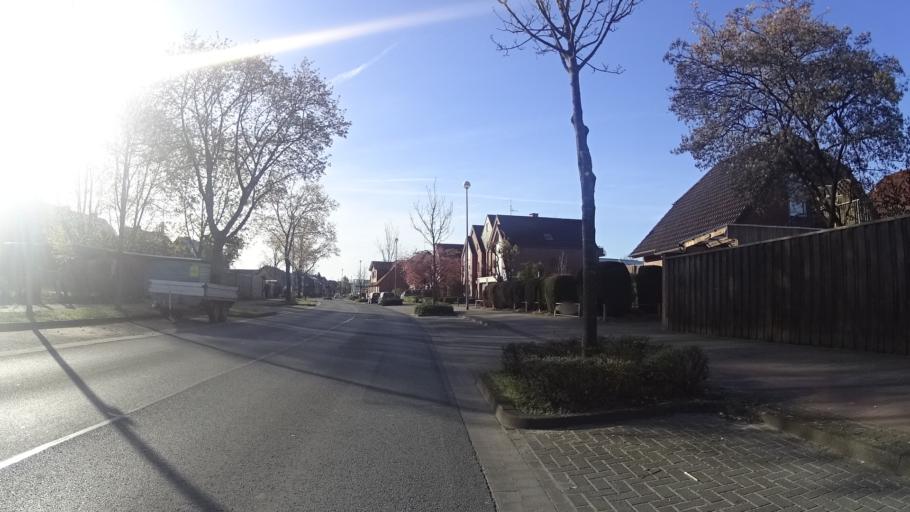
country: DE
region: North Rhine-Westphalia
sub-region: Regierungsbezirk Munster
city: Greven
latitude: 52.0982
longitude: 7.5906
